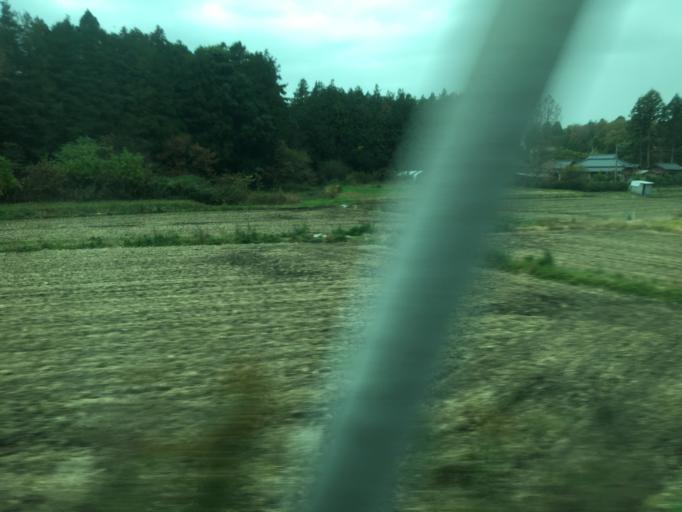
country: JP
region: Ibaraki
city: Ishioka
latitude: 36.2346
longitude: 140.2897
